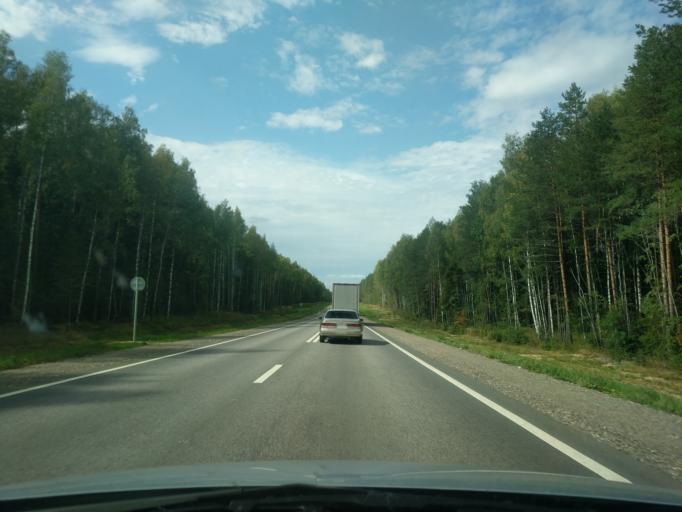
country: RU
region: Kostroma
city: Kadyy
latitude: 57.7978
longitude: 42.8351
